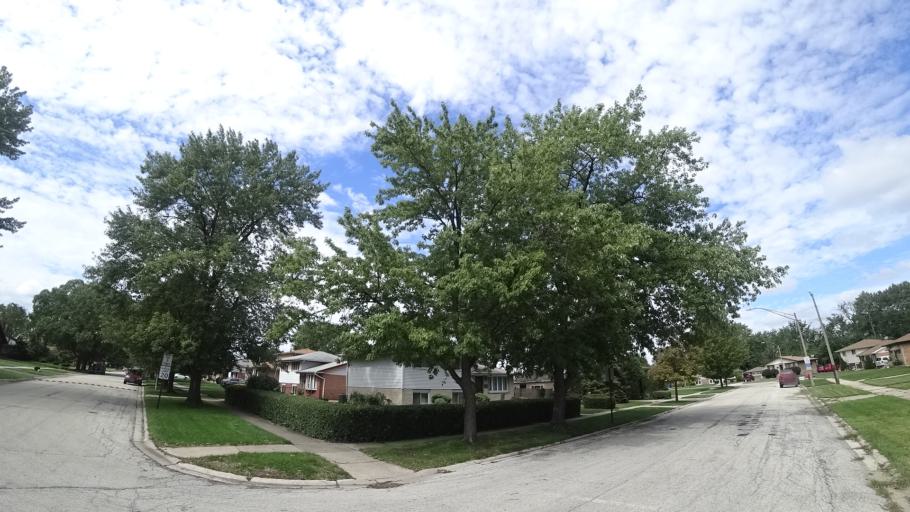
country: US
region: Illinois
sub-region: Cook County
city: Chicago Ridge
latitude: 41.7060
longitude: -87.7805
